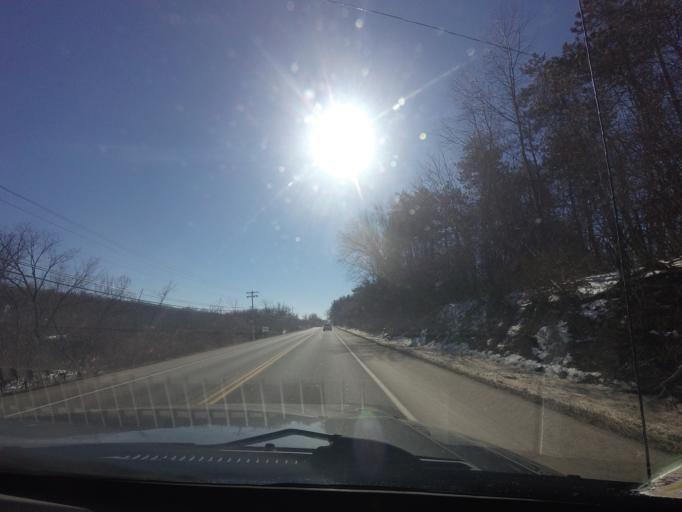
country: US
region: New York
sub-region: Saratoga County
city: Waterford
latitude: 42.7730
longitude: -73.6591
